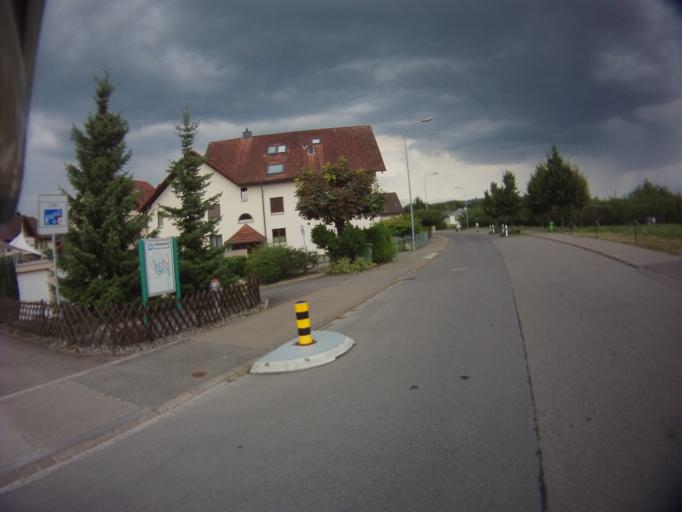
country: CH
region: Zug
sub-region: Zug
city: Hunenberg
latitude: 47.1768
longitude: 8.4237
